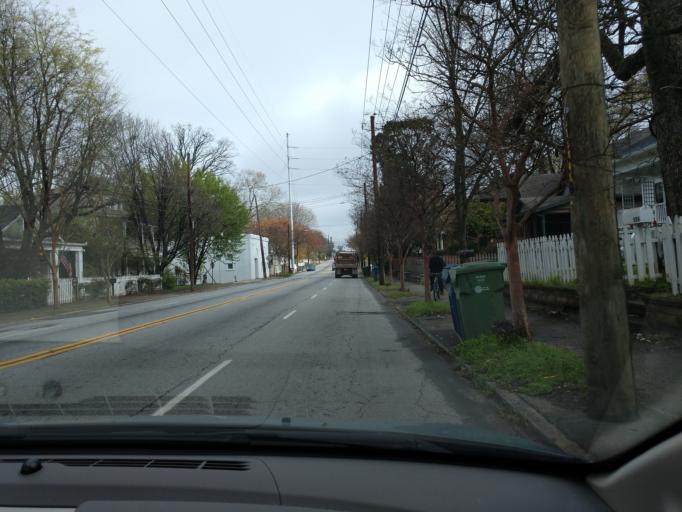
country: US
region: Georgia
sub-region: Fulton County
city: Atlanta
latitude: 33.7392
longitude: -84.3681
